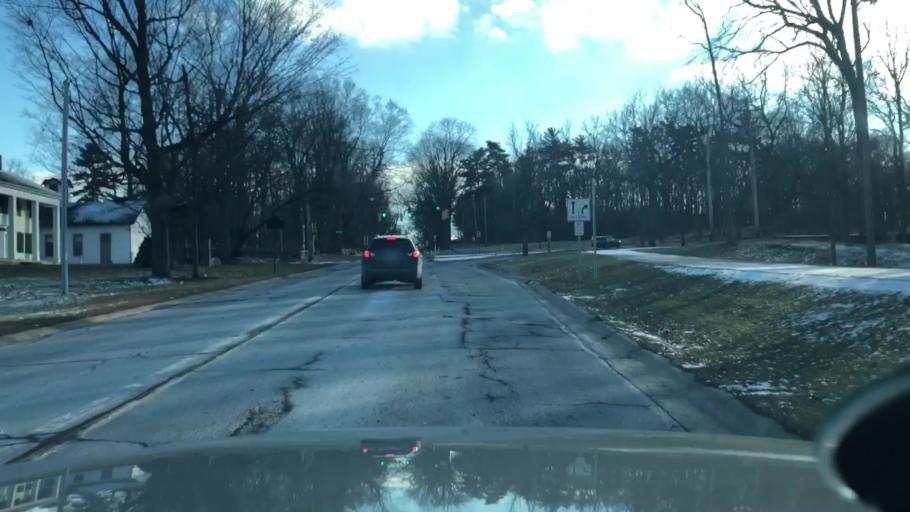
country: US
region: Michigan
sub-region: Jackson County
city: Jackson
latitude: 42.2155
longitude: -84.4182
